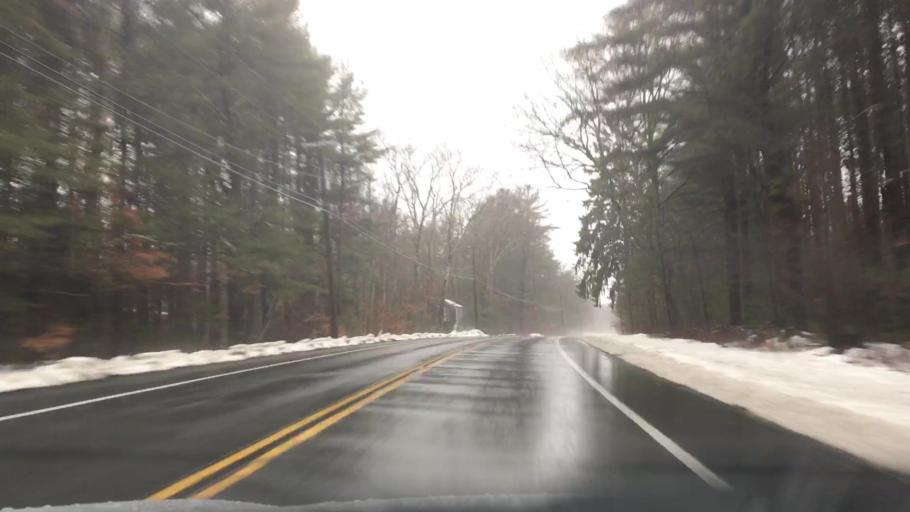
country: US
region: Massachusetts
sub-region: Hampshire County
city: Pelham
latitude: 42.3774
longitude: -72.4011
